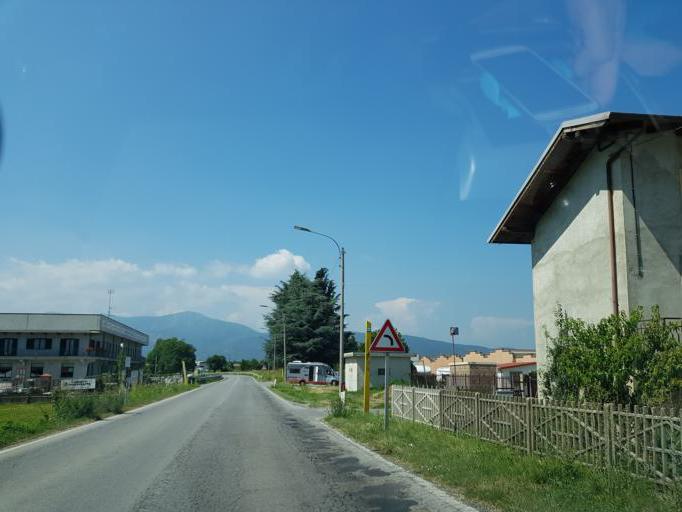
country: IT
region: Piedmont
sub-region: Provincia di Cuneo
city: Caraglio
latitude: 44.4313
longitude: 7.4236
